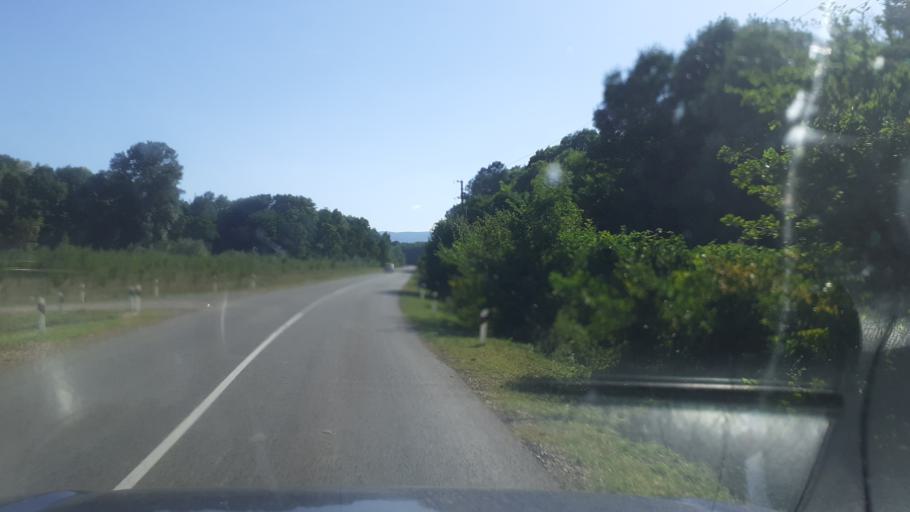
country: RU
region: Krasnodarskiy
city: Azovskaya
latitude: 44.7630
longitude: 38.5659
